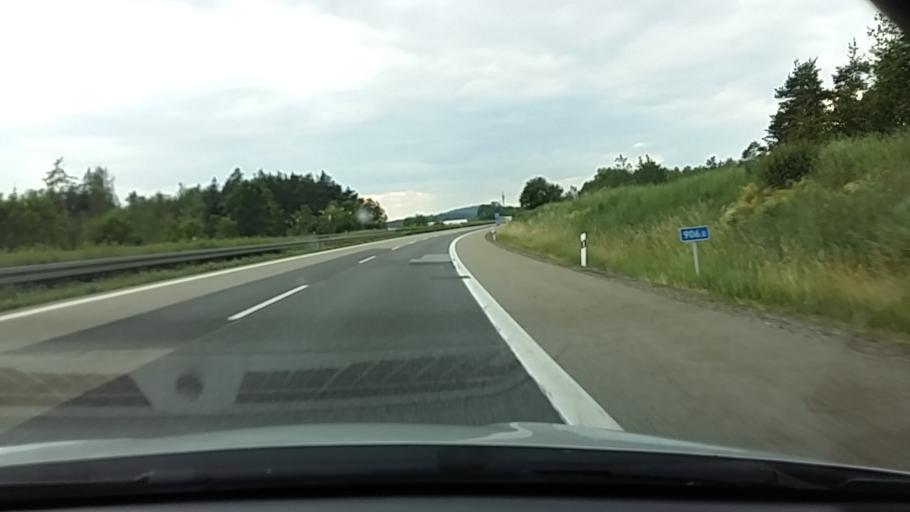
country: DE
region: Bavaria
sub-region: Upper Palatinate
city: Waidhaus
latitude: 49.6314
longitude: 12.4994
